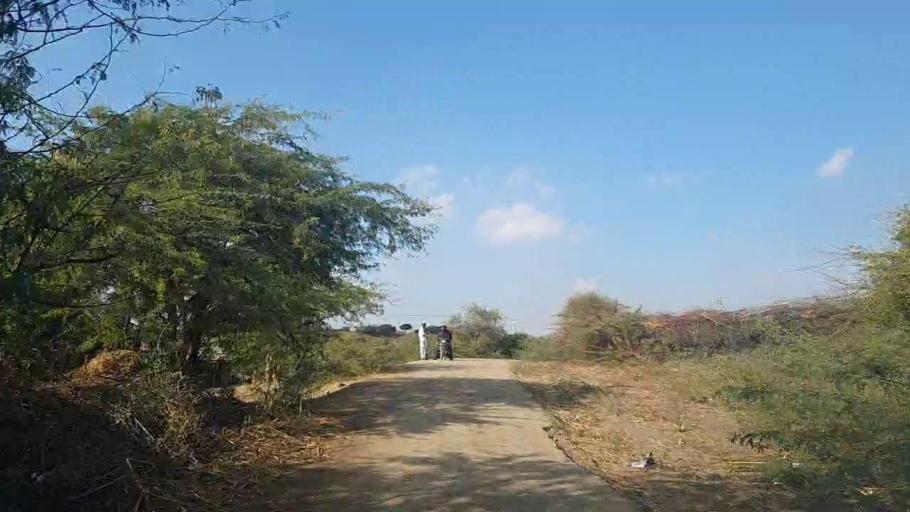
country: PK
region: Sindh
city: Tando Mittha Khan
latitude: 25.9956
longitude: 69.2440
